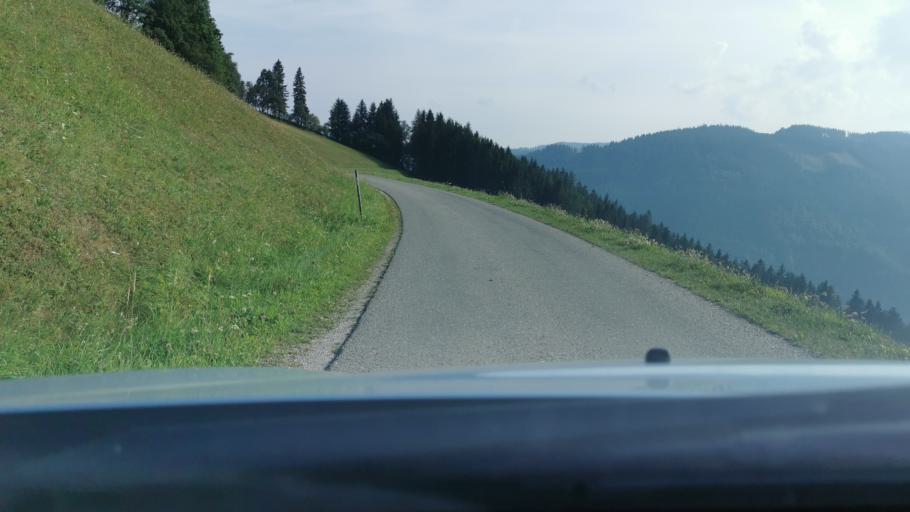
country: AT
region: Styria
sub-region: Politischer Bezirk Weiz
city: Fischbach
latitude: 47.3987
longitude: 15.6247
